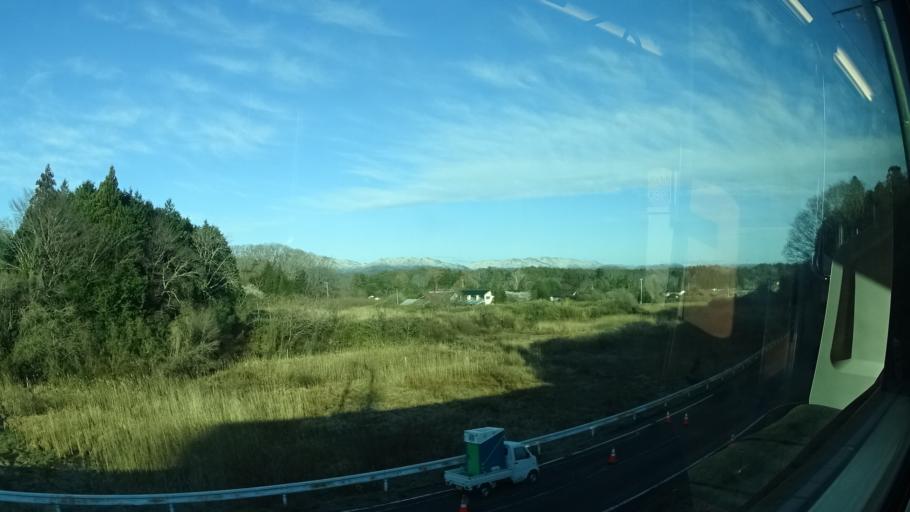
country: JP
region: Fukushima
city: Namie
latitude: 37.4296
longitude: 141.0014
